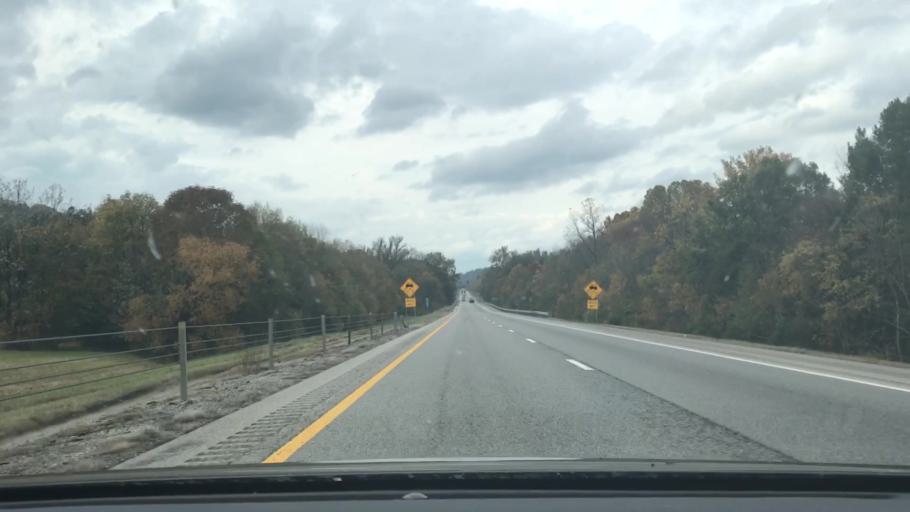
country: US
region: Tennessee
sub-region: Smith County
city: Gordonsville
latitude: 36.1486
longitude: -85.8703
